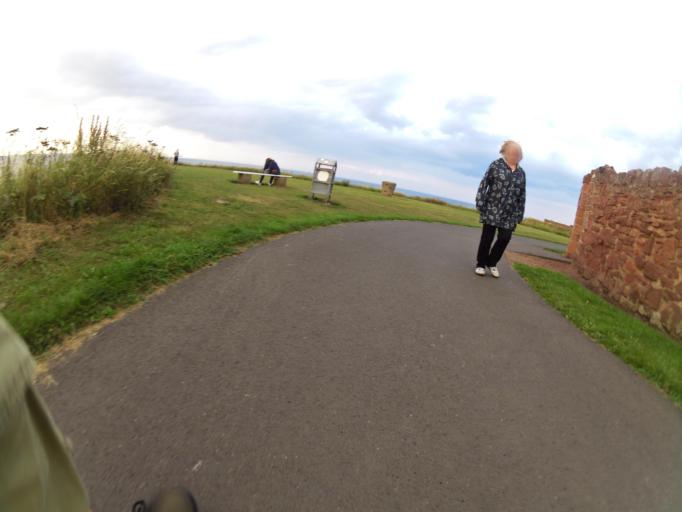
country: GB
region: Scotland
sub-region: East Lothian
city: Dunbar
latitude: 56.0058
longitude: -2.5294
